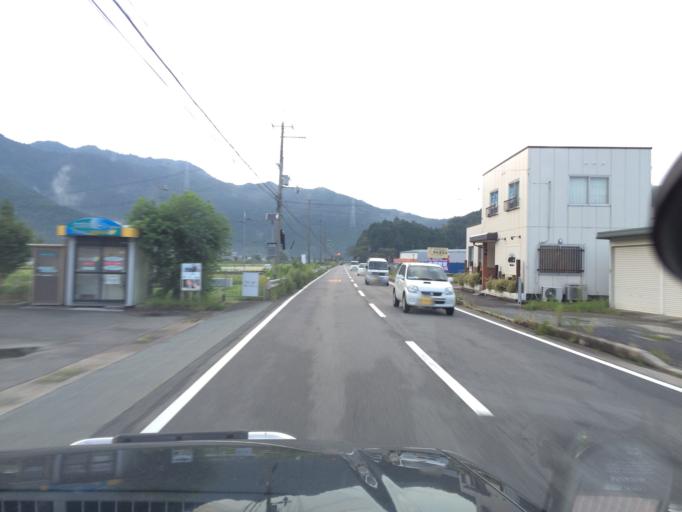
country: JP
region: Hyogo
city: Nishiwaki
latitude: 35.1068
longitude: 134.9945
